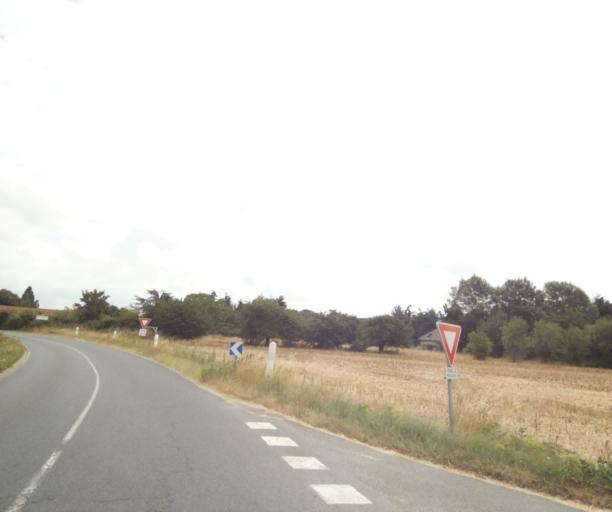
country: FR
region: Centre
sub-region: Departement du Loiret
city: Vennecy
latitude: 47.9326
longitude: 2.0425
